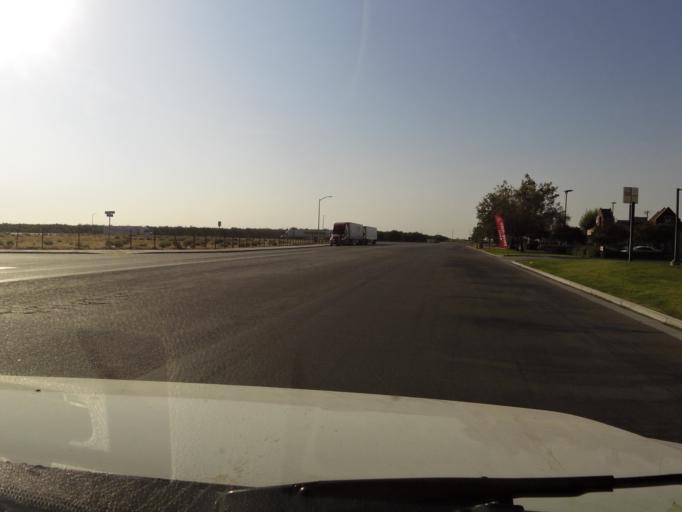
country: US
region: California
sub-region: Kern County
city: Shafter
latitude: 35.5312
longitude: -119.1870
